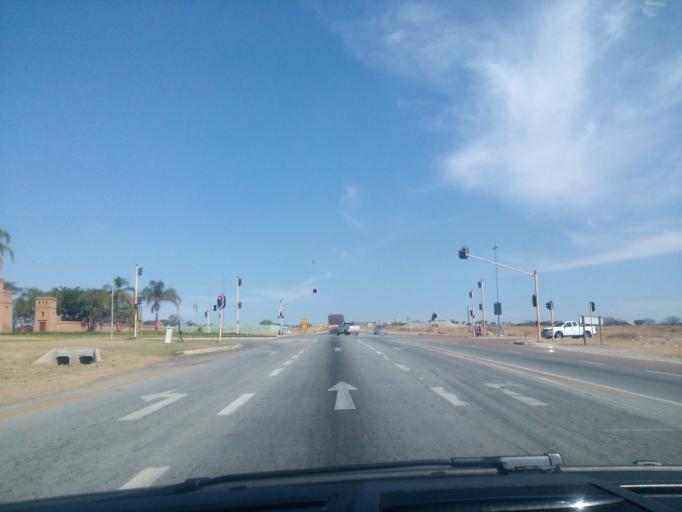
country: ZA
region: Limpopo
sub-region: Capricorn District Municipality
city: Polokwane
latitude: -23.9419
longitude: 29.4214
